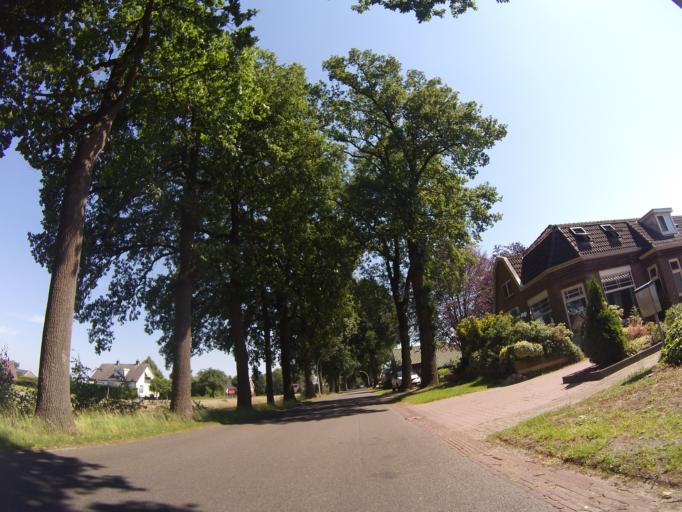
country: NL
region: Drenthe
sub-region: Gemeente Borger-Odoorn
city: Borger
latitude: 52.8479
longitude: 6.7617
